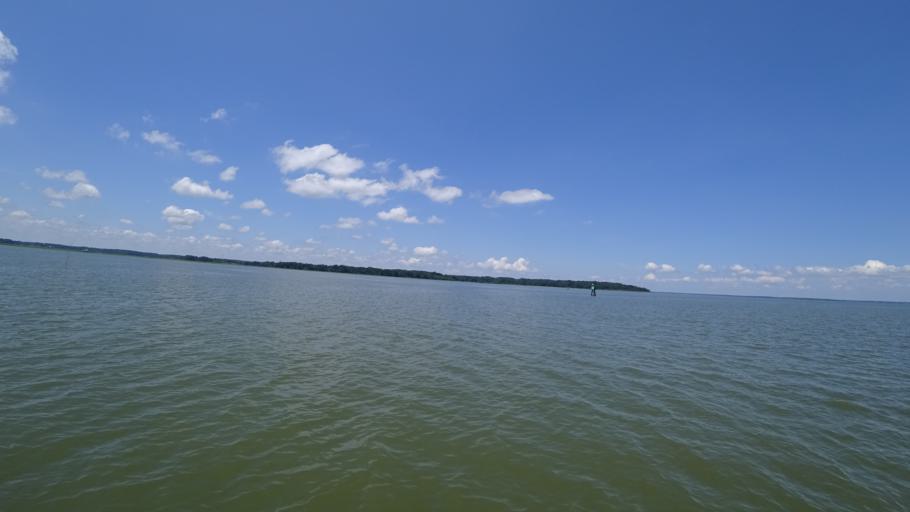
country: US
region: Virginia
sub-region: Isle of Wight County
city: Carrollton
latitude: 37.0022
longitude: -76.5725
